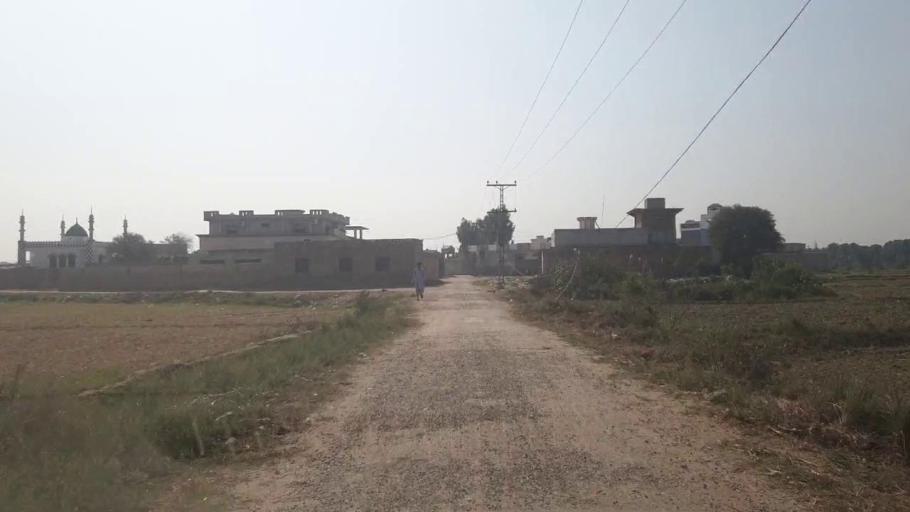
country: PK
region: Sindh
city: Tando Allahyar
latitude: 25.4797
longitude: 68.7910
